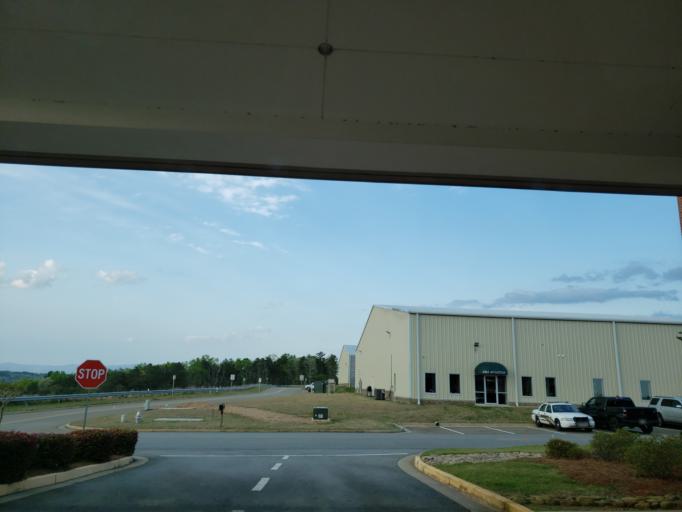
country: US
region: Georgia
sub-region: Cherokee County
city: Ball Ground
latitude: 34.3089
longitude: -84.4284
